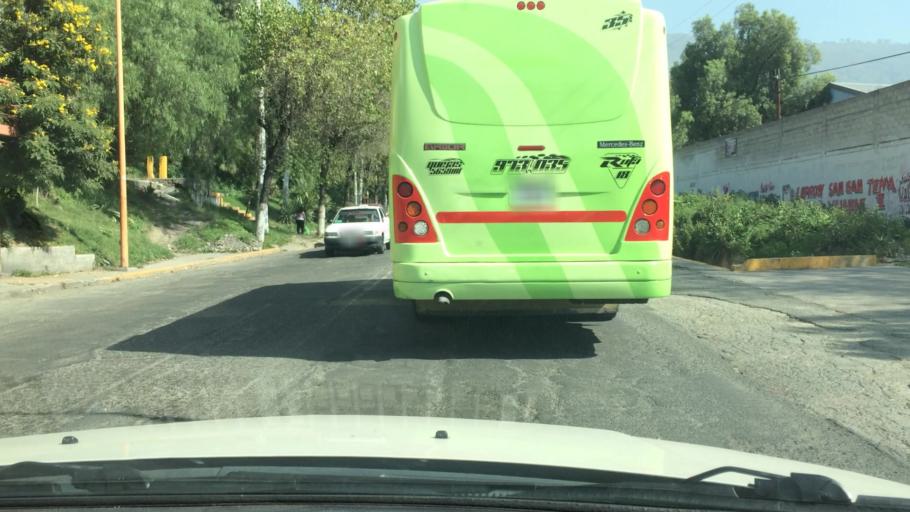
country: MX
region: Mexico
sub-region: Tlalnepantla de Baz
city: Puerto Escondido (Tepeolulco Puerto Escondido)
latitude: 19.5280
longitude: -99.1201
